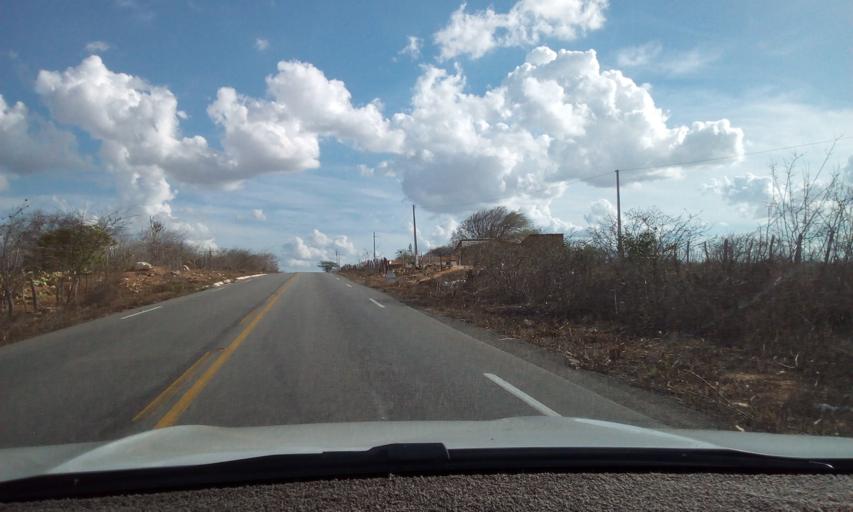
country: BR
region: Paraiba
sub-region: Soledade
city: Soledade
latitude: -6.8824
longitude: -36.3992
